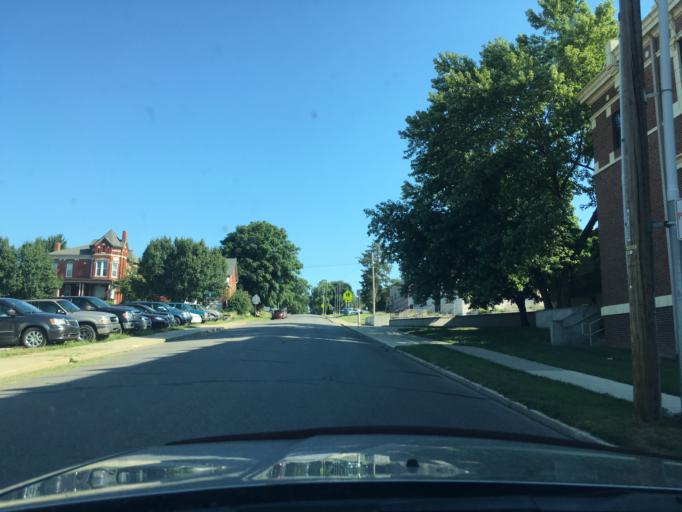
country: US
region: Kansas
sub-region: Atchison County
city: Atchison
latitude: 39.5645
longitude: -95.1204
